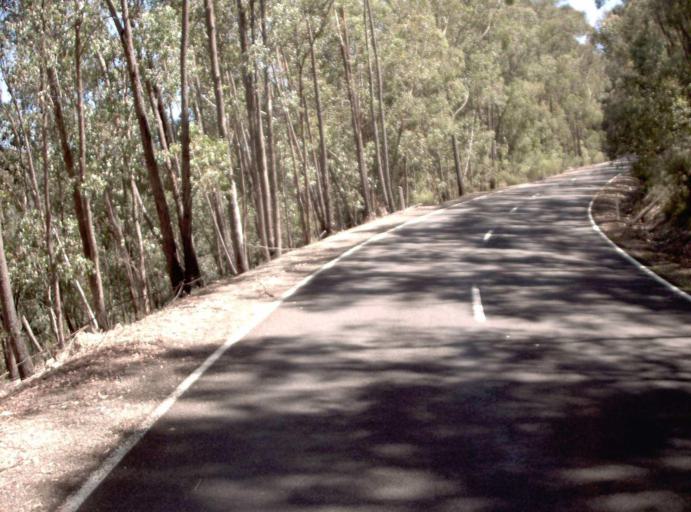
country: AU
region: Victoria
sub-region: East Gippsland
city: Lakes Entrance
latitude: -37.3846
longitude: 148.2187
